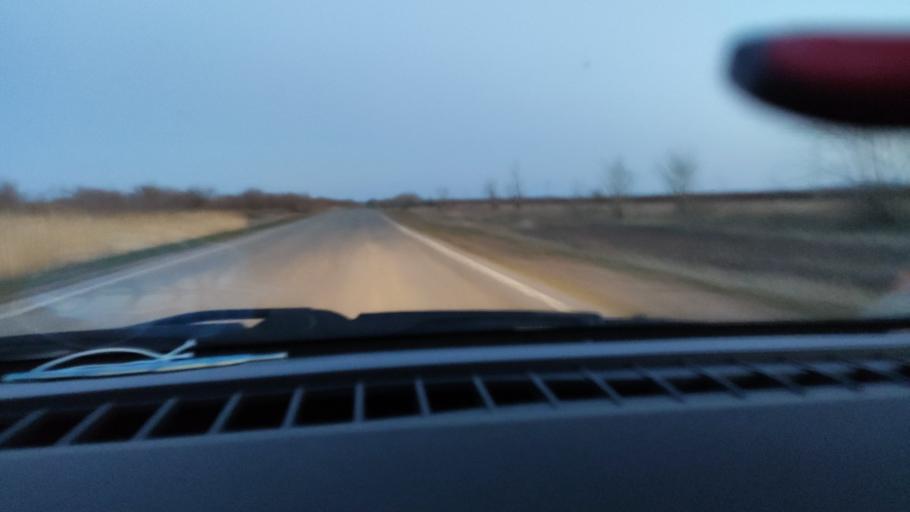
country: RU
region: Saratov
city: Rovnoye
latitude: 51.0042
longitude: 46.1022
